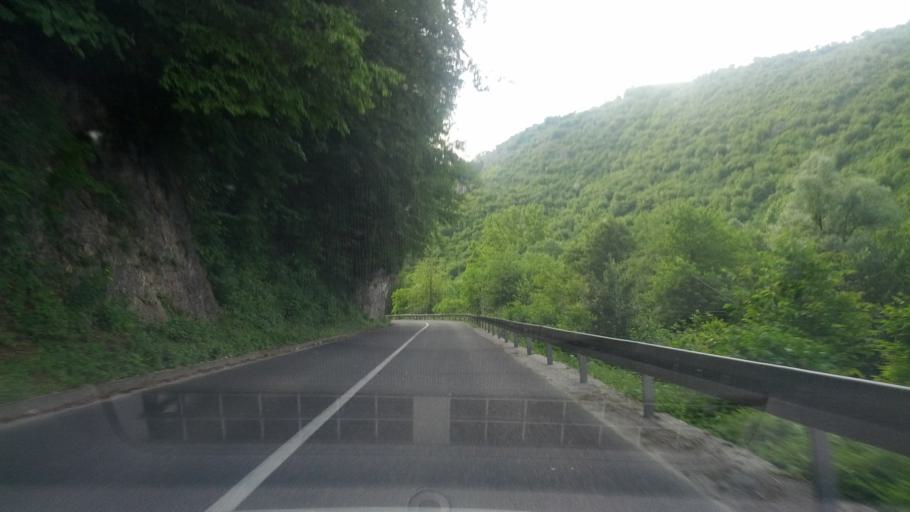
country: BA
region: Federation of Bosnia and Herzegovina
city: Ostrozac
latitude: 44.9092
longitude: 15.9754
